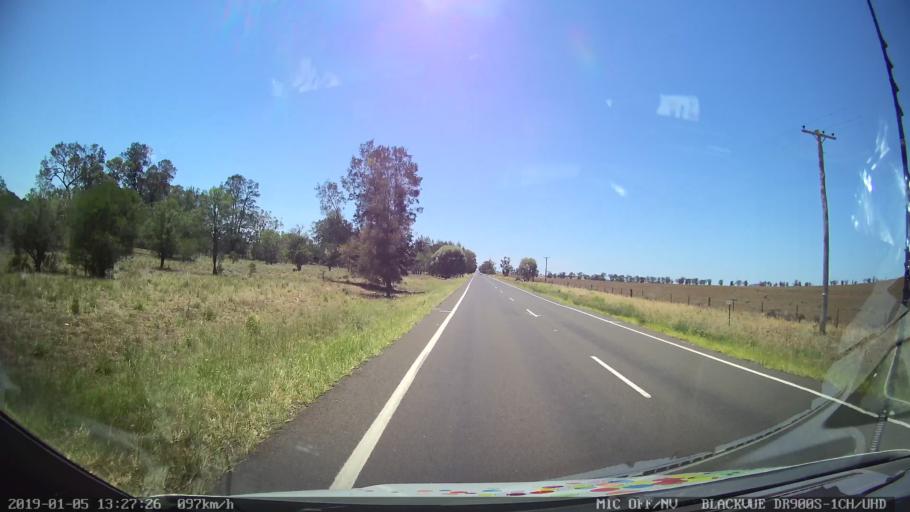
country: AU
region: New South Wales
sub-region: Gunnedah
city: Gunnedah
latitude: -31.0446
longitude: 150.0292
